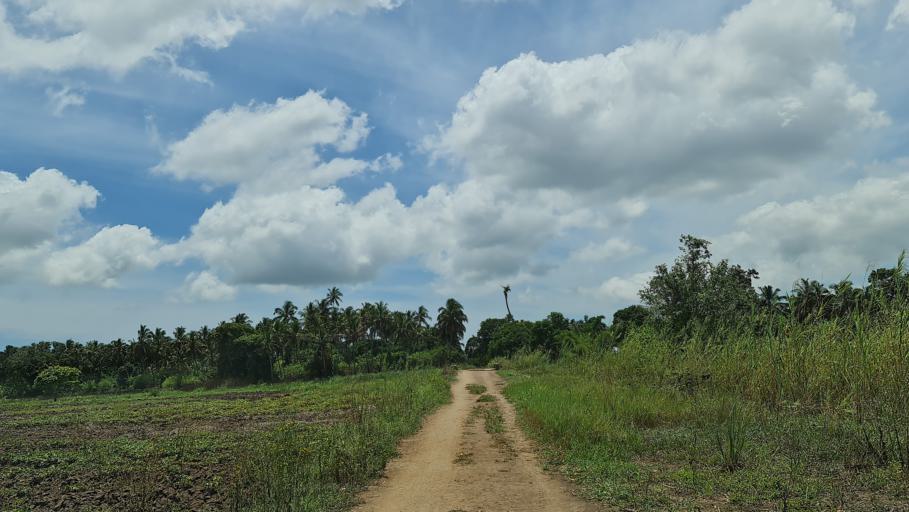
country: MZ
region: Zambezia
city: Quelimane
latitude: -17.5750
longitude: 37.3741
